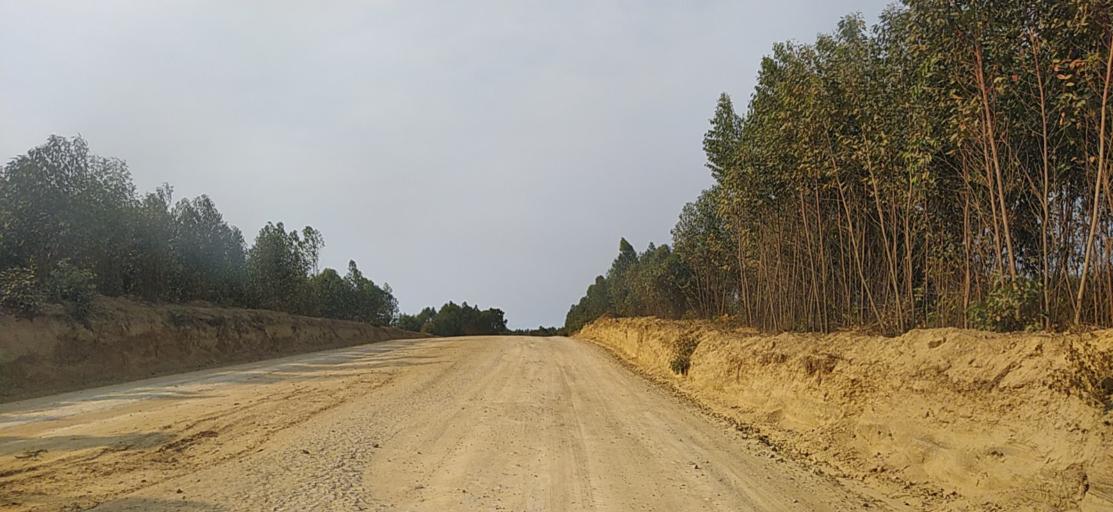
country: MG
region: Alaotra Mangoro
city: Moramanga
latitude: -18.6571
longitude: 48.2743
